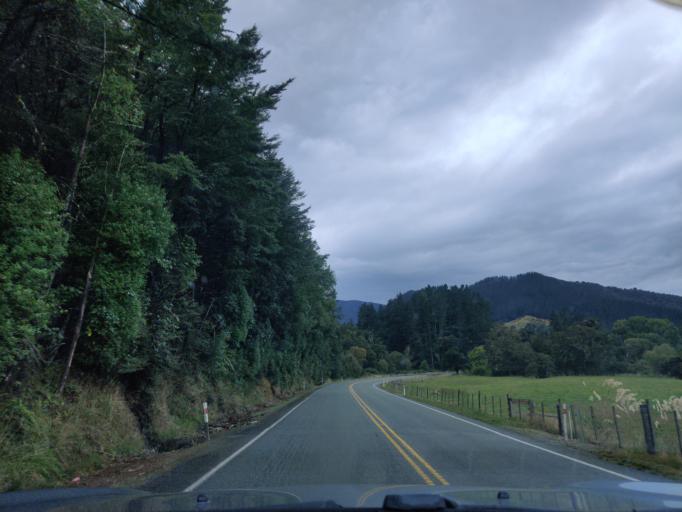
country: NZ
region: Tasman
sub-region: Tasman District
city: Wakefield
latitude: -41.6925
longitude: 172.4896
